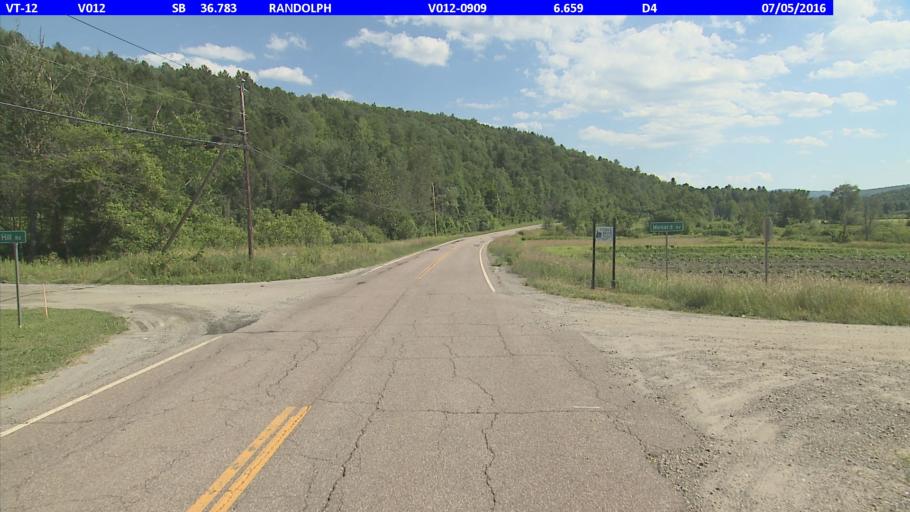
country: US
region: Vermont
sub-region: Orange County
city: Randolph
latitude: 43.9831
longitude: -72.6483
